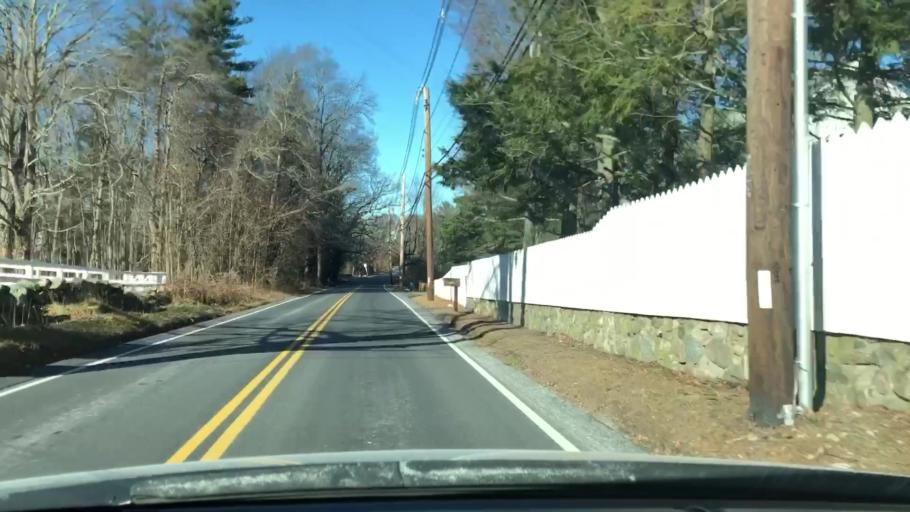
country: US
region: Massachusetts
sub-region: Norfolk County
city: Westwood
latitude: 42.1902
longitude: -71.2485
